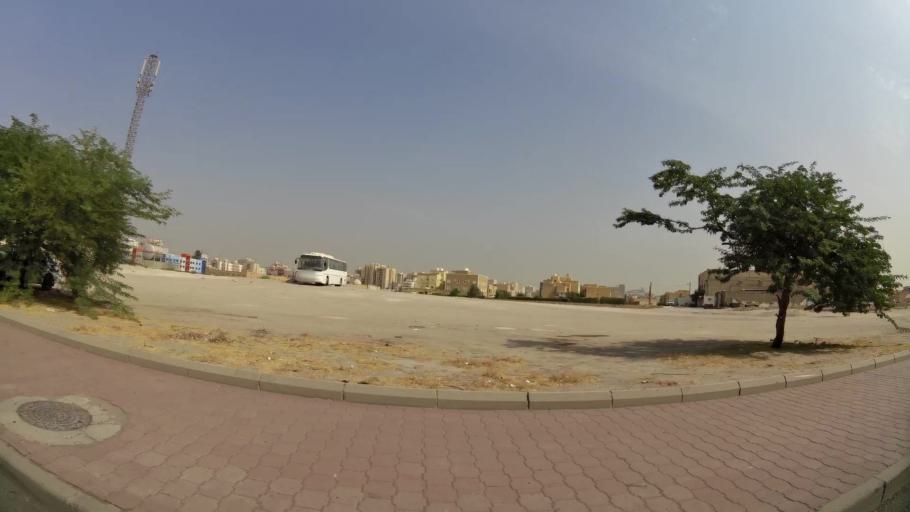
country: KW
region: Al Farwaniyah
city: Al Farwaniyah
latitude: 29.2499
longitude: 47.9299
